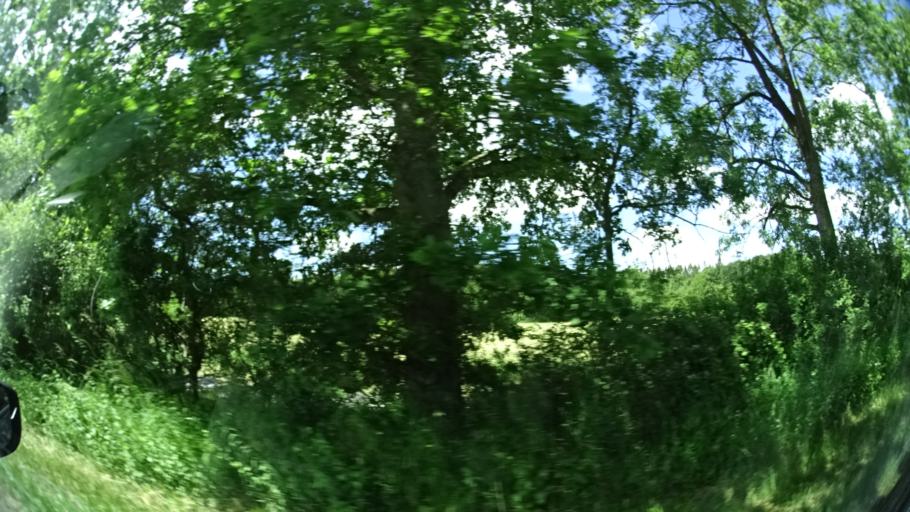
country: DK
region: Central Jutland
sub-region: Syddjurs Kommune
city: Ronde
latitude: 56.2878
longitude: 10.4806
